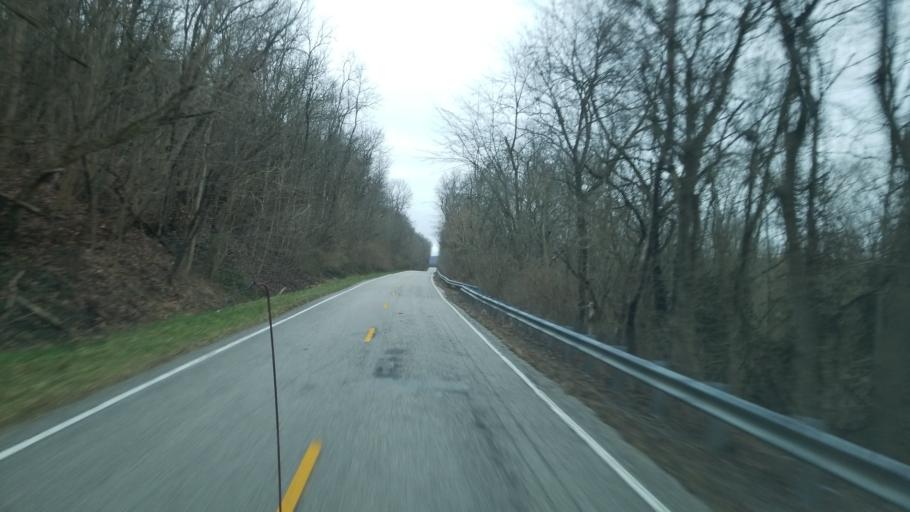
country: US
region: Kentucky
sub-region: Bracken County
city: Brooksville
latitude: 38.7785
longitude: -84.1295
